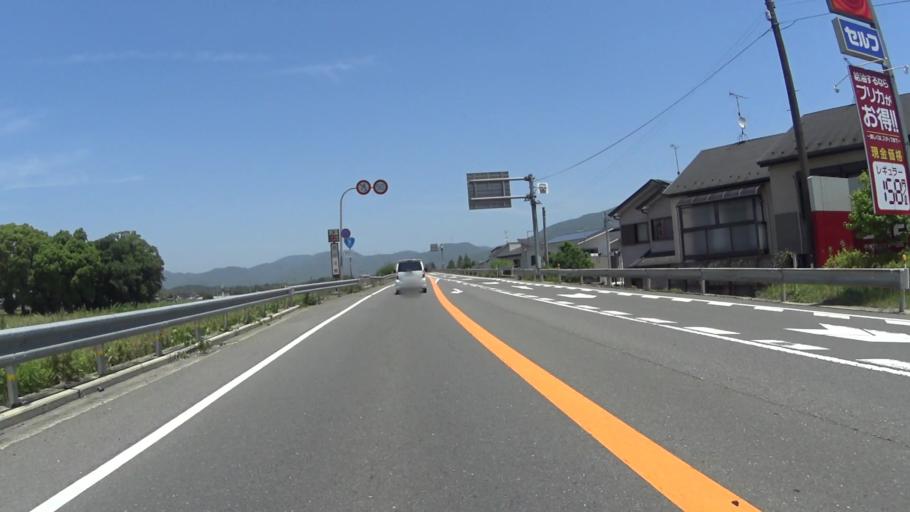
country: JP
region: Kyoto
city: Kameoka
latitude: 35.0510
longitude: 135.5456
